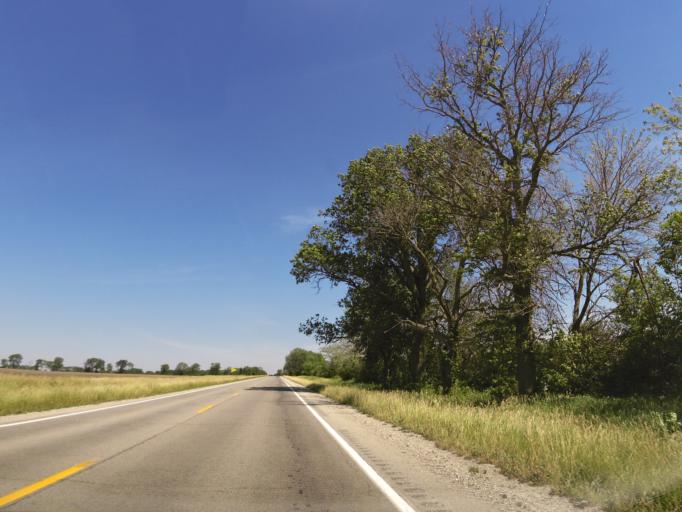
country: US
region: Illinois
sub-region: Vermilion County
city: Danville
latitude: 40.2509
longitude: -87.6472
